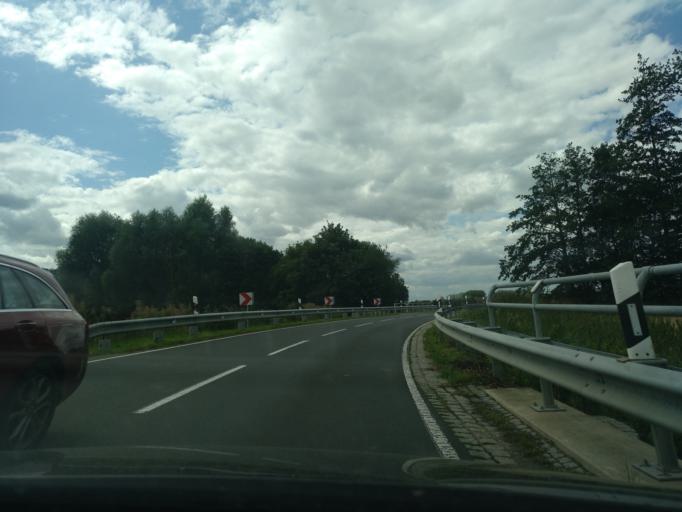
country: DE
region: Lower Saxony
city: Sickte
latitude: 52.2032
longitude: 10.6241
